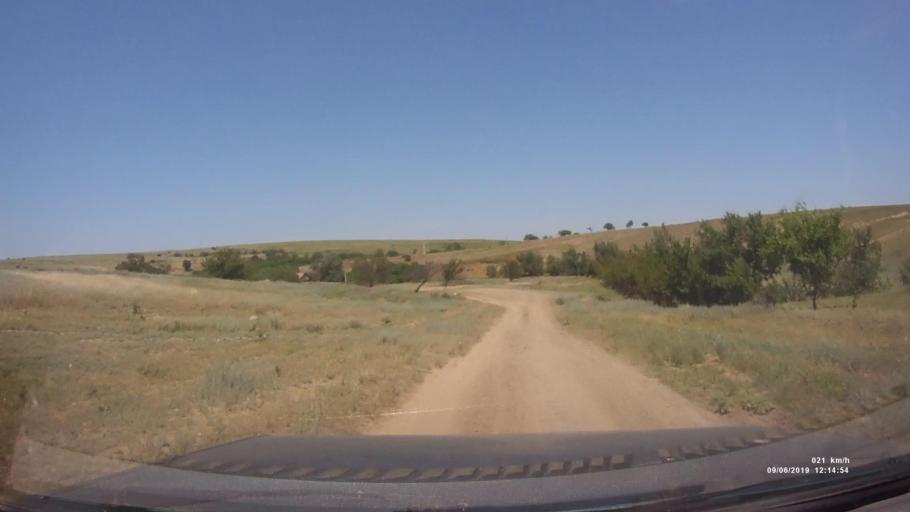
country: RU
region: Rostov
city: Staraya Stanitsa
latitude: 48.2531
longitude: 40.3231
